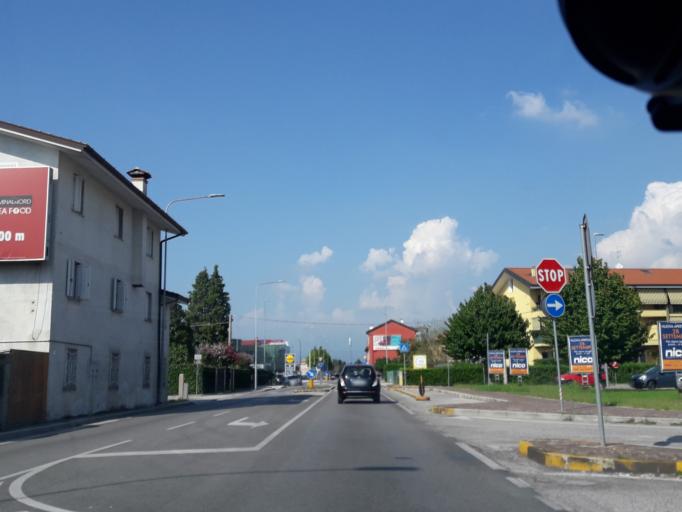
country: IT
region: Friuli Venezia Giulia
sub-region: Provincia di Udine
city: Feletto Umberto
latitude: 46.0902
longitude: 13.2322
